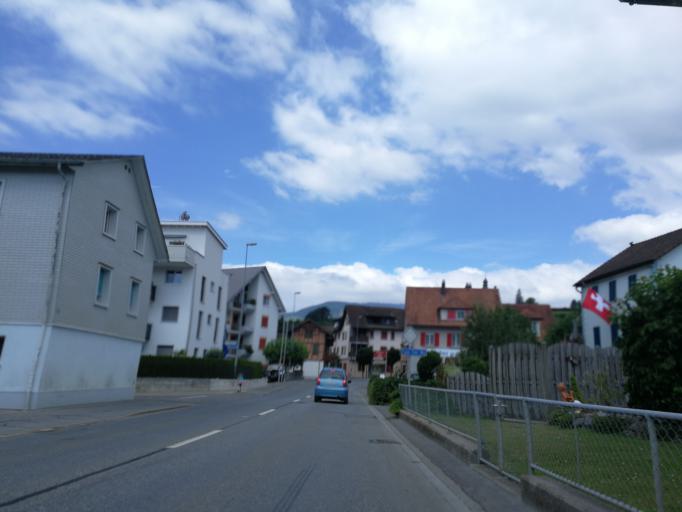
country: CH
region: Saint Gallen
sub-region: Wahlkreis See-Gaster
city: Benken
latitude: 47.1974
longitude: 9.0025
